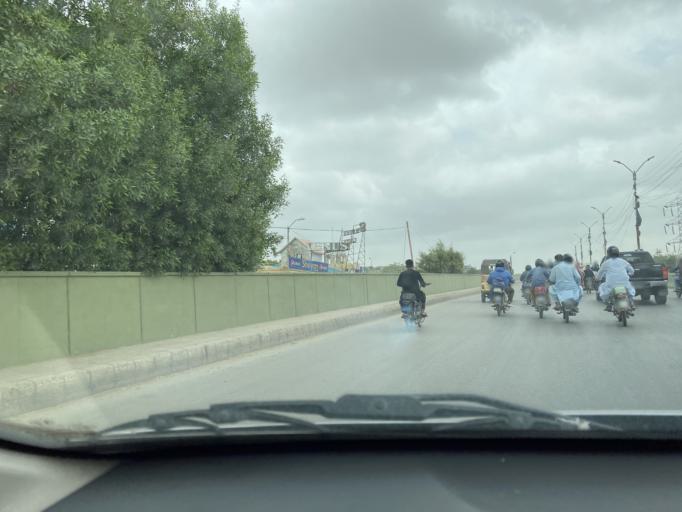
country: PK
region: Sindh
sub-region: Karachi District
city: Karachi
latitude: 24.8645
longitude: 67.0853
